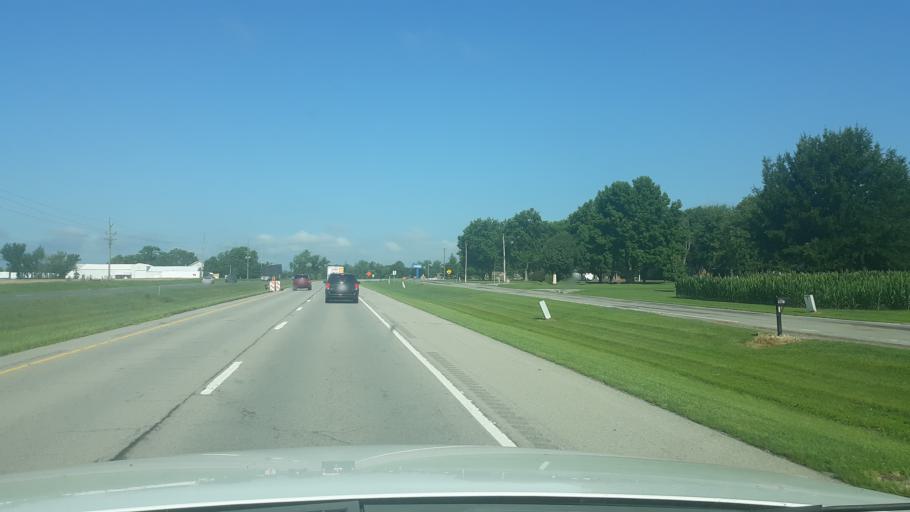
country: US
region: Illinois
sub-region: Williamson County
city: Marion
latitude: 37.7299
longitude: -88.8792
